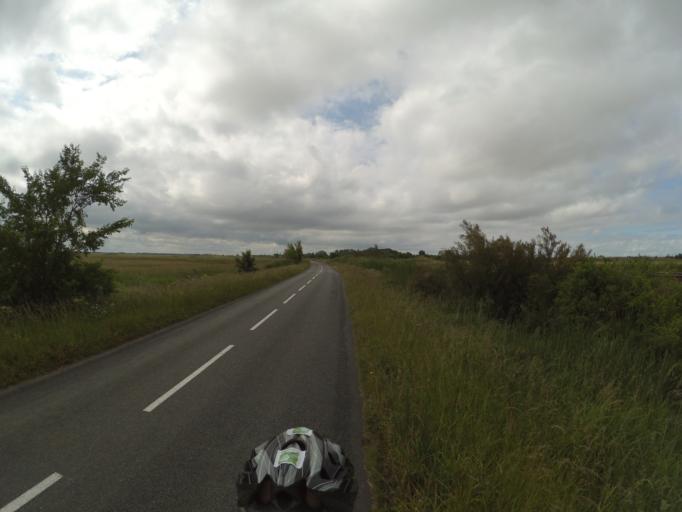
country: FR
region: Poitou-Charentes
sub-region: Departement de la Charente-Maritime
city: Yves
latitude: 46.0294
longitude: -1.0482
